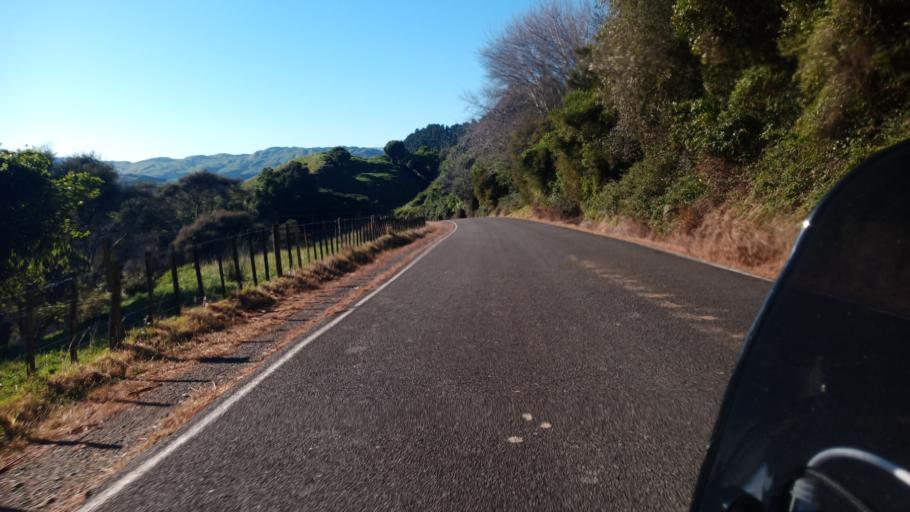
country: NZ
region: Hawke's Bay
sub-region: Wairoa District
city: Wairoa
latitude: -38.8267
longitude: 177.2918
